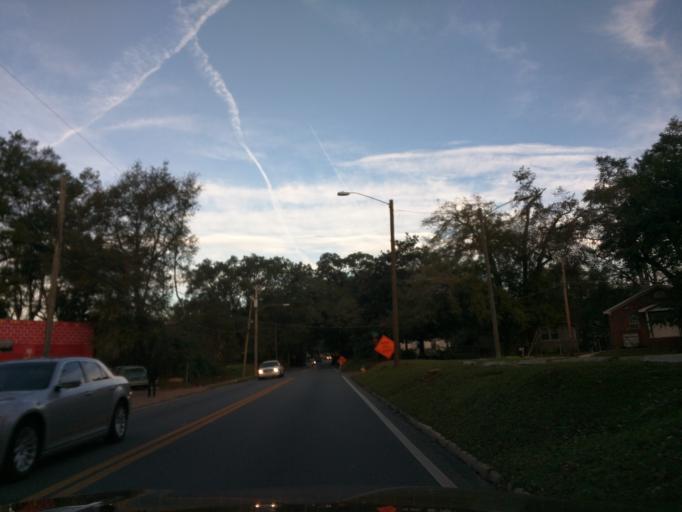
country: US
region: Florida
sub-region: Leon County
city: Tallahassee
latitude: 30.4545
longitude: -84.2932
